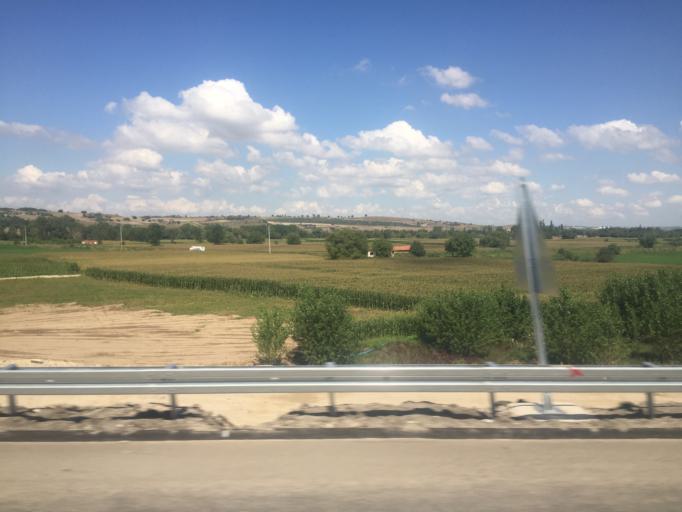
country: TR
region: Balikesir
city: Gobel
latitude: 39.9847
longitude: 28.1823
